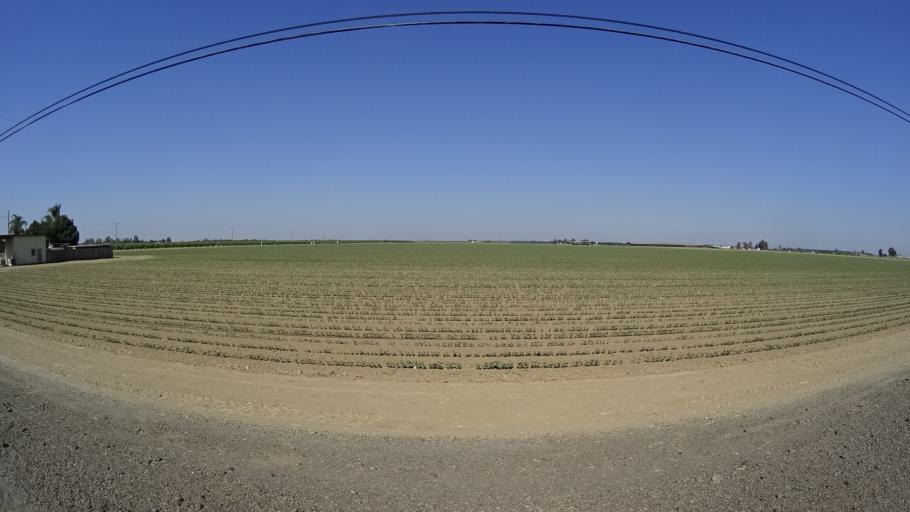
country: US
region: California
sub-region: Kings County
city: Hanford
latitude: 36.3513
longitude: -119.5651
